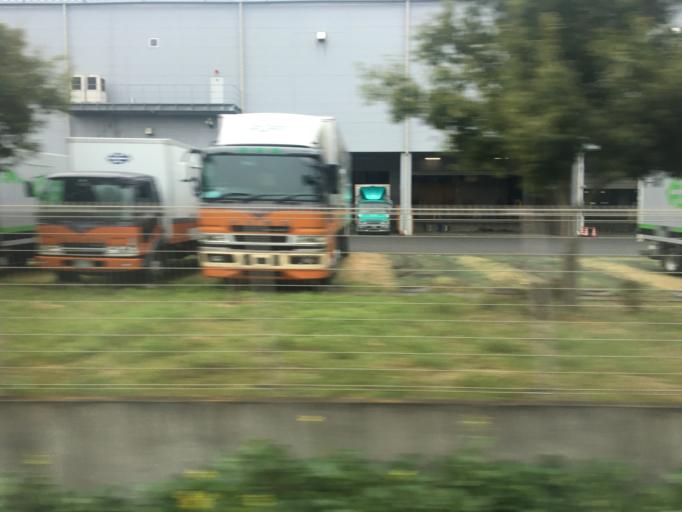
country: JP
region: Saitama
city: Hanno
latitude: 35.8012
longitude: 139.3334
